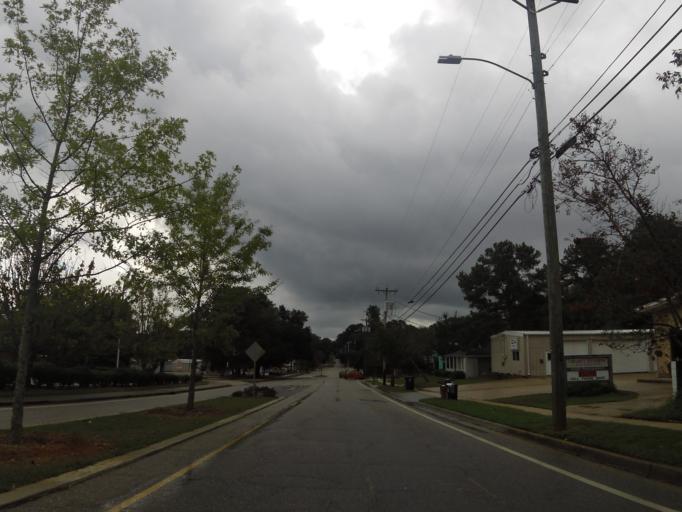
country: US
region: Alabama
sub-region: Baldwin County
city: Fairhope
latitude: 30.5230
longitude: -87.9001
